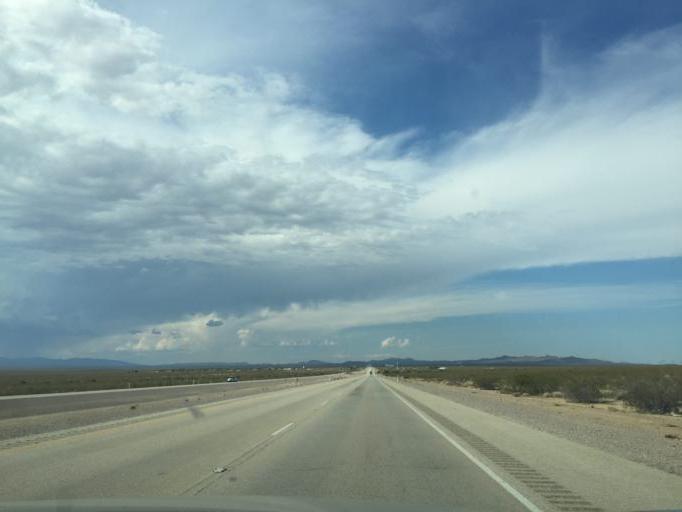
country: US
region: Nevada
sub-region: Clark County
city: Laughlin
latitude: 35.2794
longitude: -114.8740
